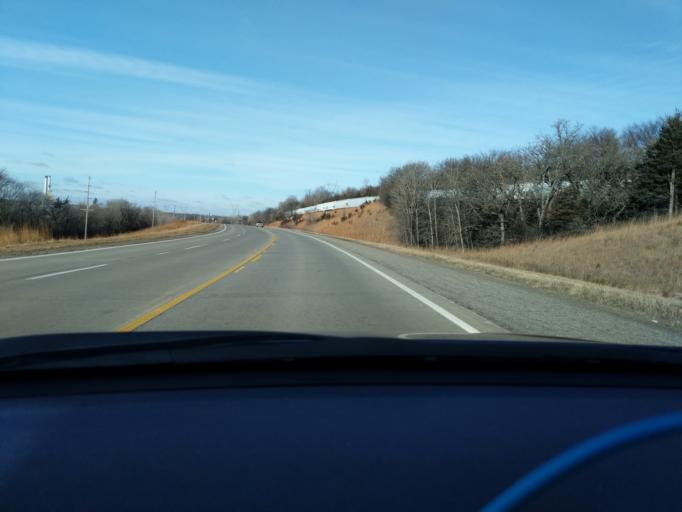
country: US
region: Minnesota
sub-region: Yellow Medicine County
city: Granite Falls
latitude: 44.8010
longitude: -95.5112
